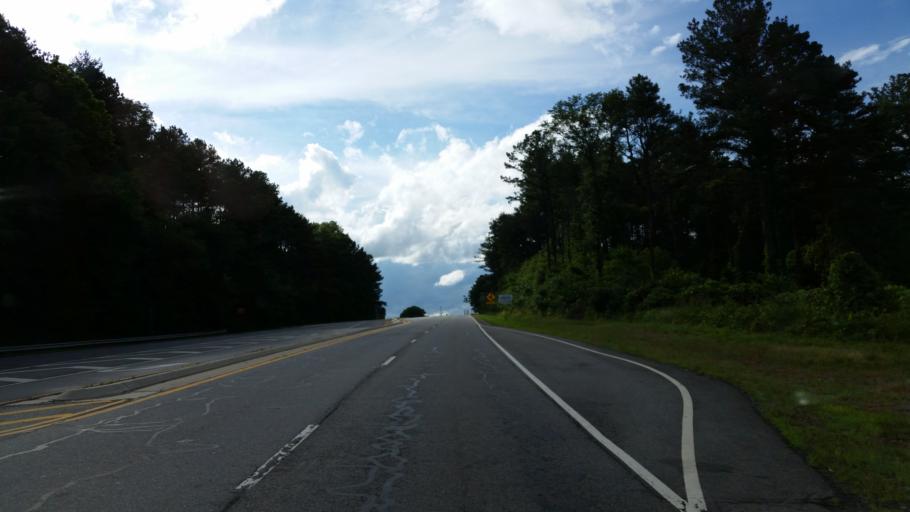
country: US
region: Georgia
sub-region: Bartow County
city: Cartersville
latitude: 34.1552
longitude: -84.7828
